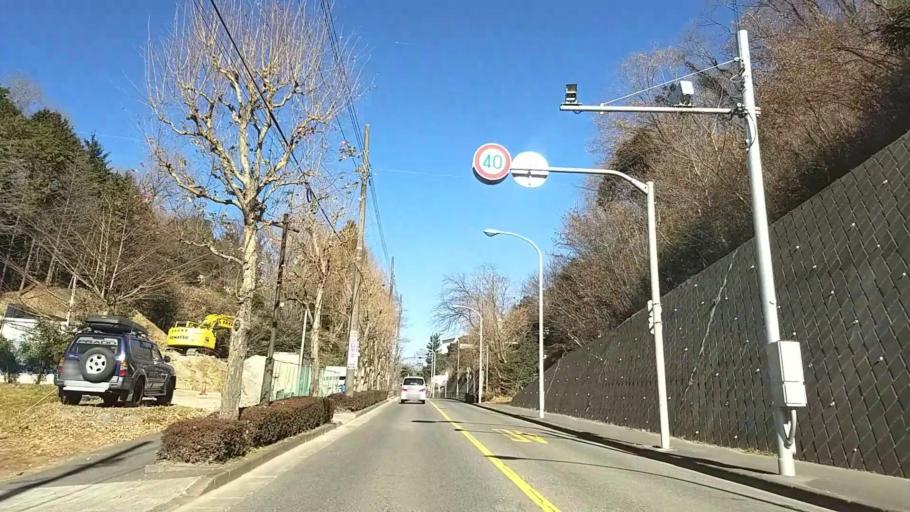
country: JP
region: Tokyo
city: Hachioji
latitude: 35.6209
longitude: 139.2874
